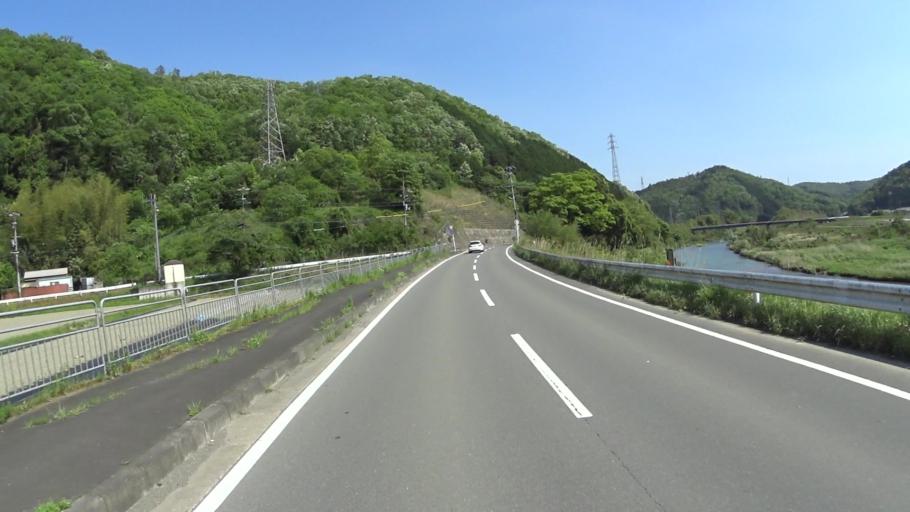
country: JP
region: Kyoto
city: Kameoka
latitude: 35.1251
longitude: 135.5045
